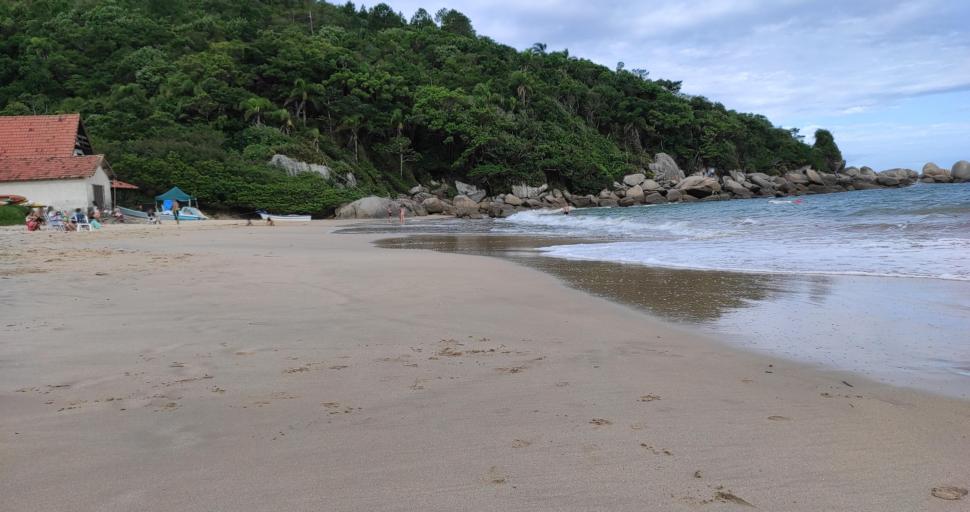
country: BR
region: Santa Catarina
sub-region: Porto Belo
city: Porto Belo
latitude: -27.2159
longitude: -48.5094
